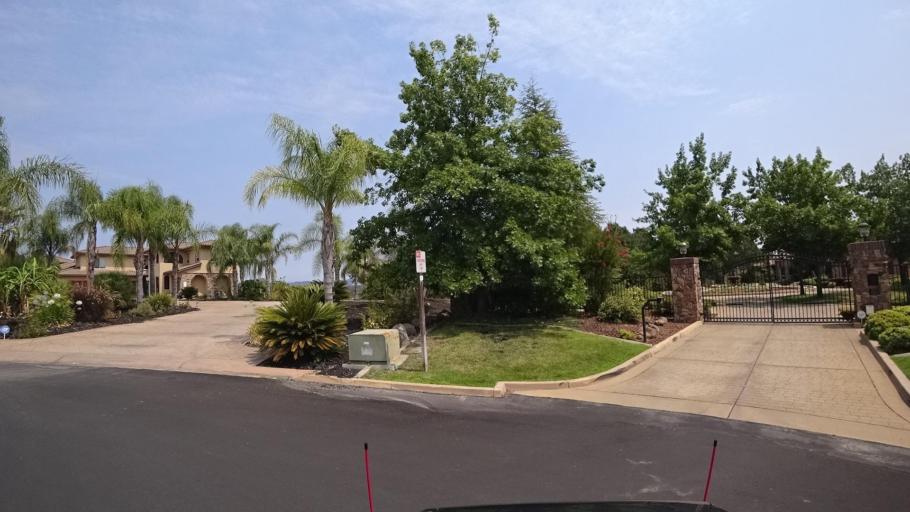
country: US
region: California
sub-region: Placer County
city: Rocklin
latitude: 38.7675
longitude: -121.2201
